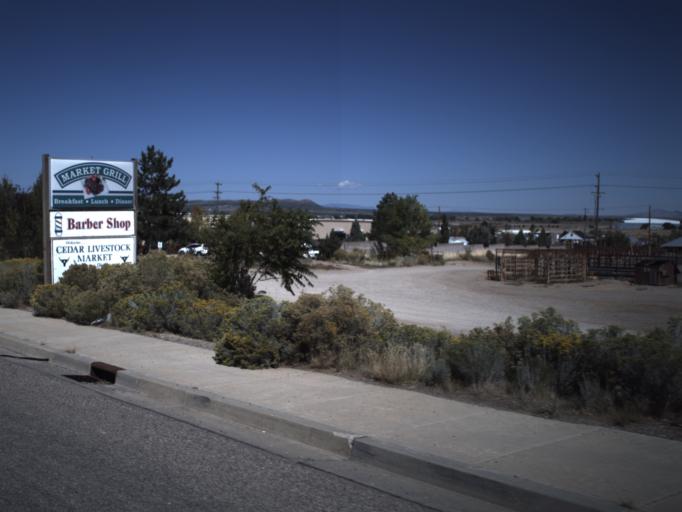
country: US
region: Utah
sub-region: Iron County
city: Cedar City
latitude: 37.6837
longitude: -113.0934
